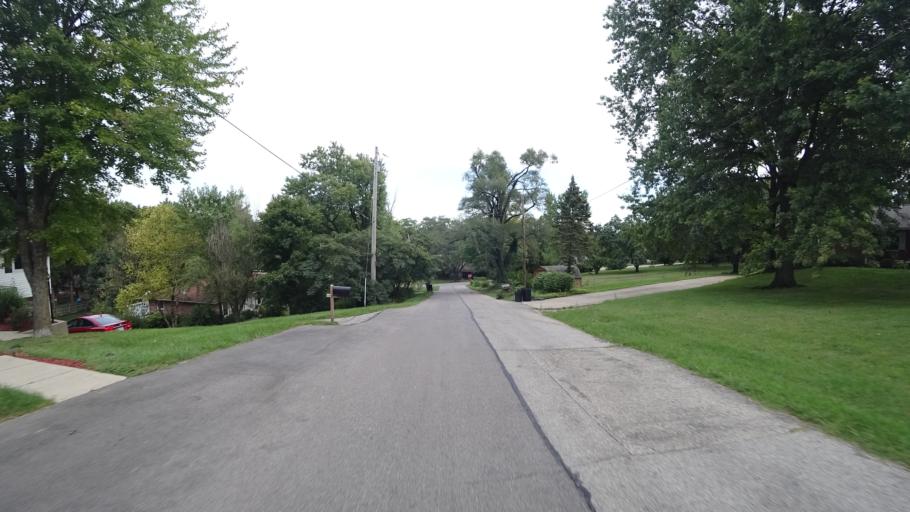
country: US
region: Ohio
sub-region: Butler County
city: New Miami
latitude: 39.4073
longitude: -84.5285
